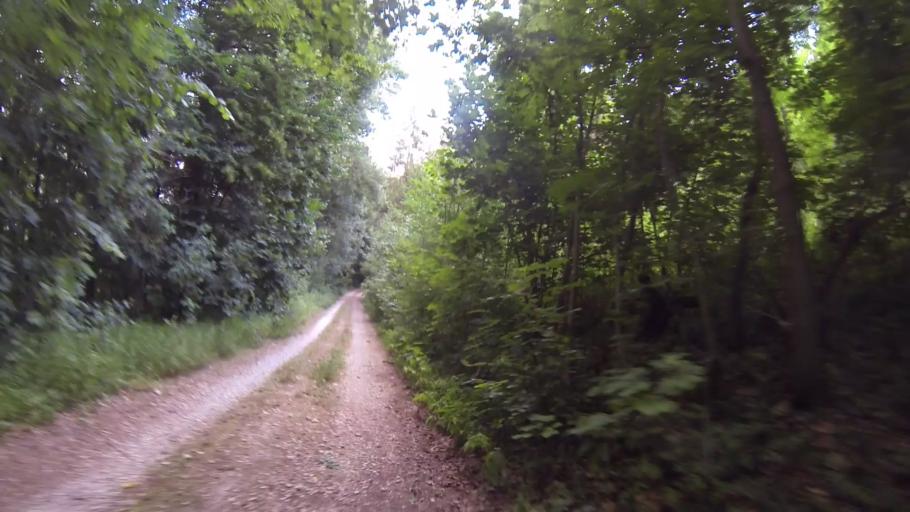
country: DE
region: Baden-Wuerttemberg
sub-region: Tuebingen Region
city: Dornstadt
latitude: 48.4338
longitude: 9.8770
